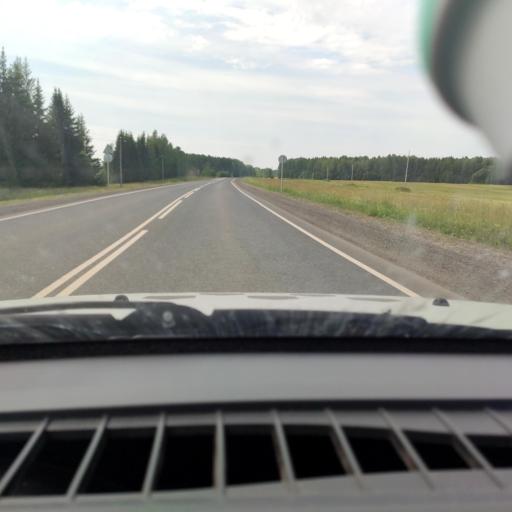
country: RU
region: Perm
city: Siva
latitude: 58.4868
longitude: 54.0654
